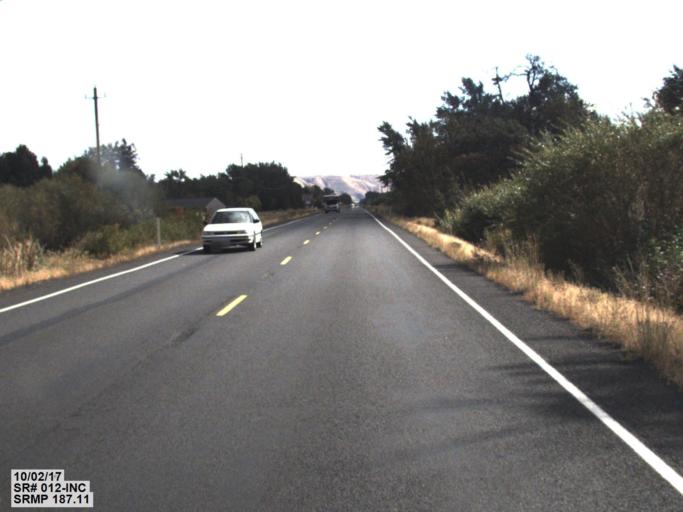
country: US
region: Washington
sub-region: Yakima County
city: Tieton
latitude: 46.7433
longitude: -120.7540
